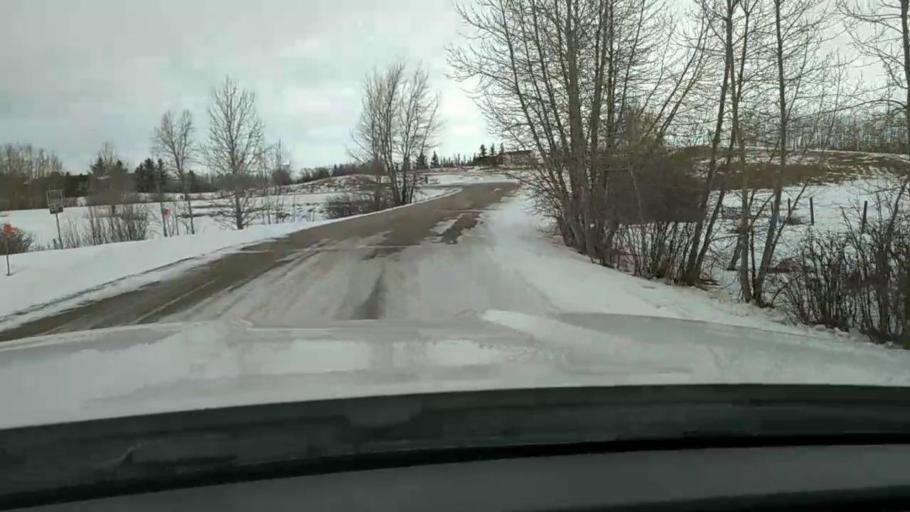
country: CA
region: Alberta
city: Cochrane
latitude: 51.1993
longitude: -114.2863
